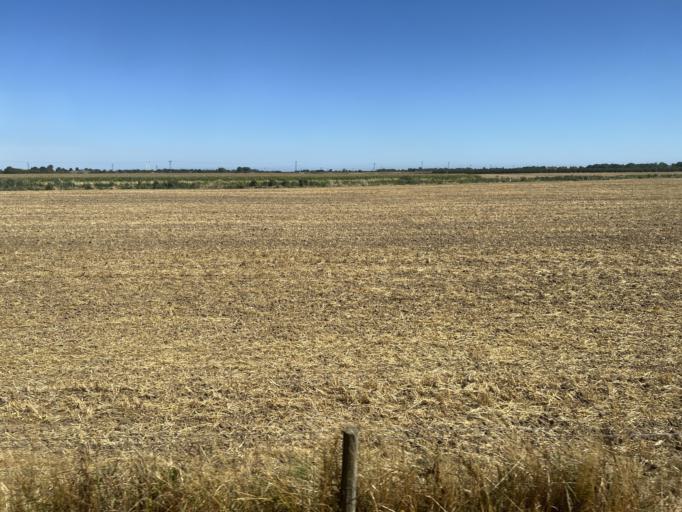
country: GB
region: England
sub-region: Lincolnshire
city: Wainfleet All Saints
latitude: 53.1132
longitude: 0.2173
